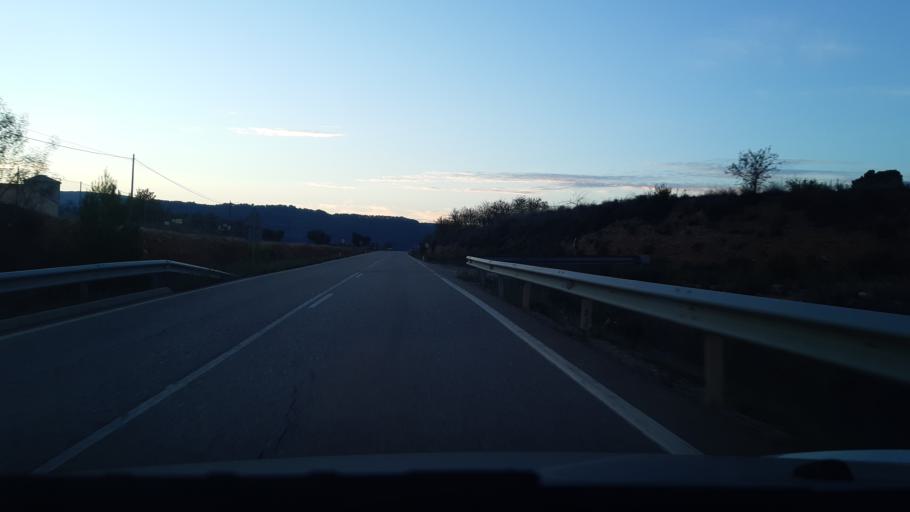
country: ES
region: Aragon
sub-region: Provincia de Teruel
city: Valderrobres
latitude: 40.8637
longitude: 0.1685
